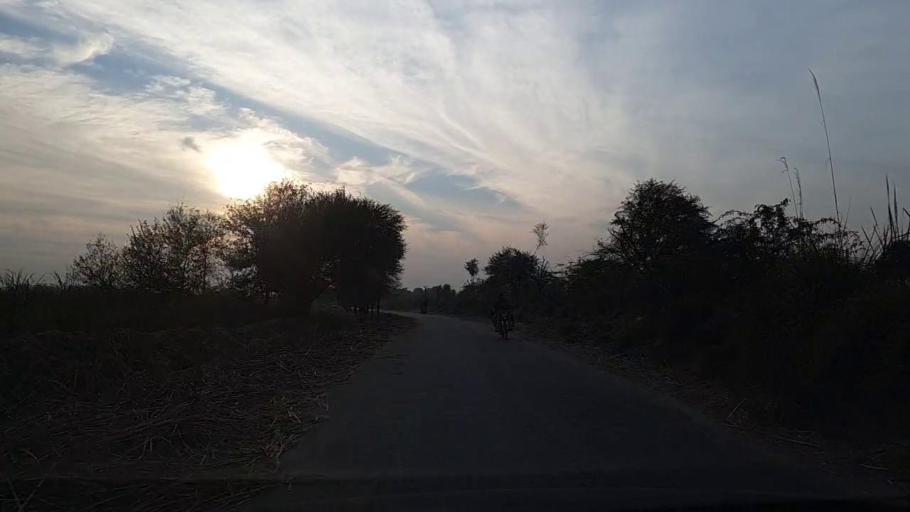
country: PK
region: Sindh
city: Daur
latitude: 26.3969
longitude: 68.4500
